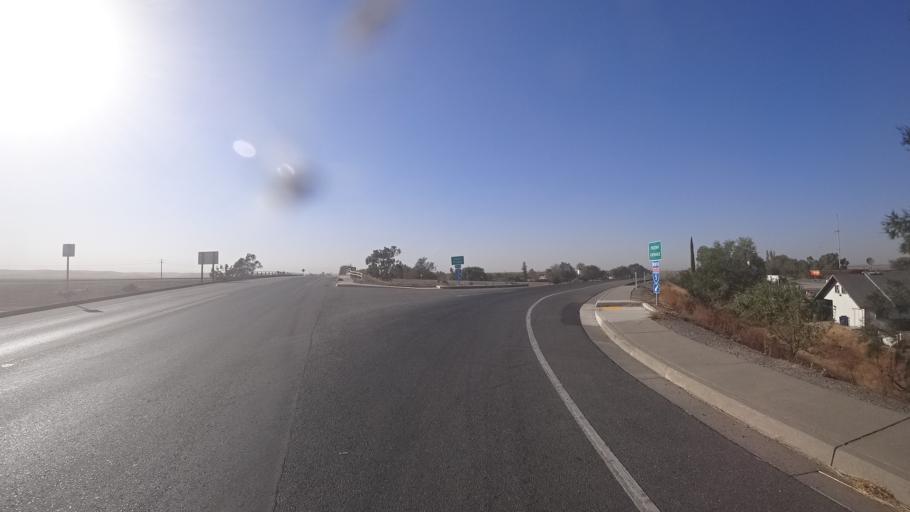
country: US
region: California
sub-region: Yolo County
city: Dunnigan
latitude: 38.7942
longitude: -121.8783
